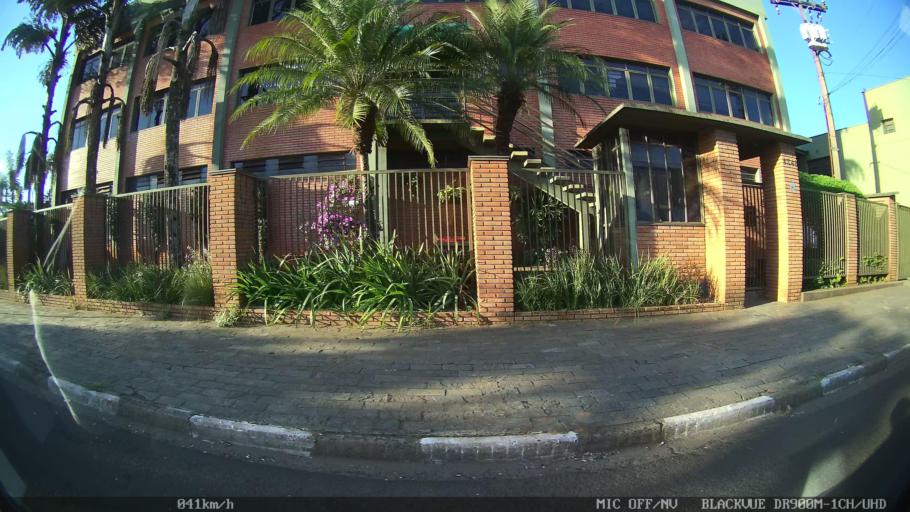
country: BR
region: Sao Paulo
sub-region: Franca
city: Franca
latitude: -20.5100
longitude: -47.3912
